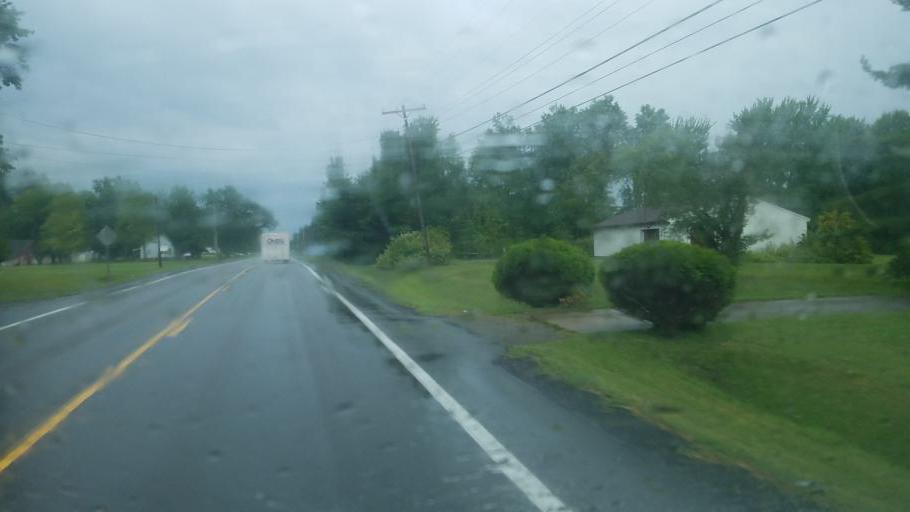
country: US
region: Ohio
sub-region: Trumbull County
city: Champion Heights
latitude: 41.3472
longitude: -80.8580
